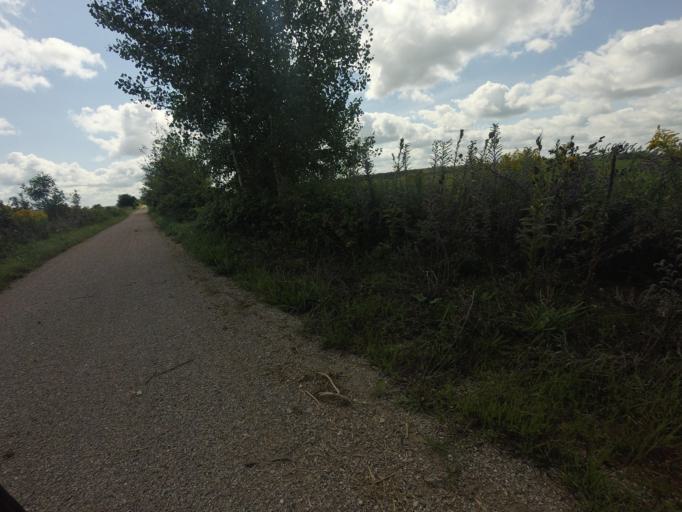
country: CA
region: Ontario
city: Huron East
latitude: 43.6430
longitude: -81.2092
